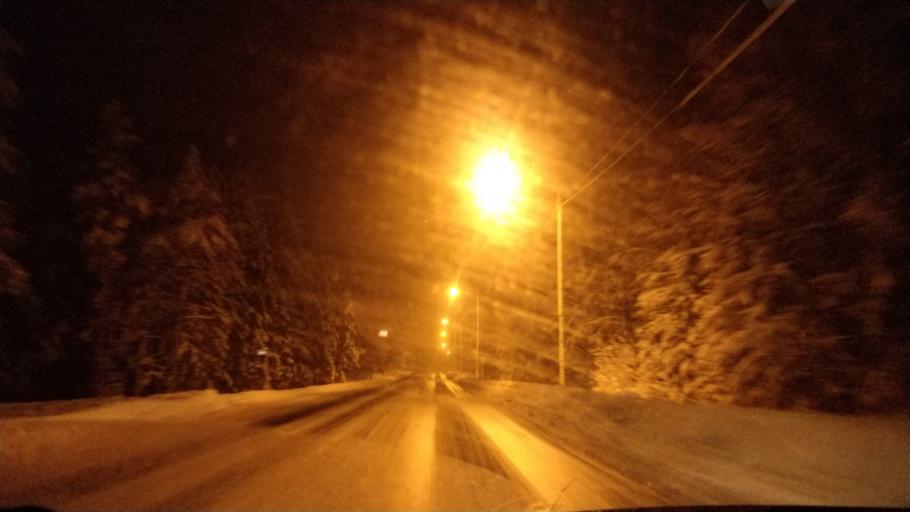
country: FI
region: Lapland
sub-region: Rovaniemi
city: Rovaniemi
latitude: 66.4179
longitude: 25.4147
